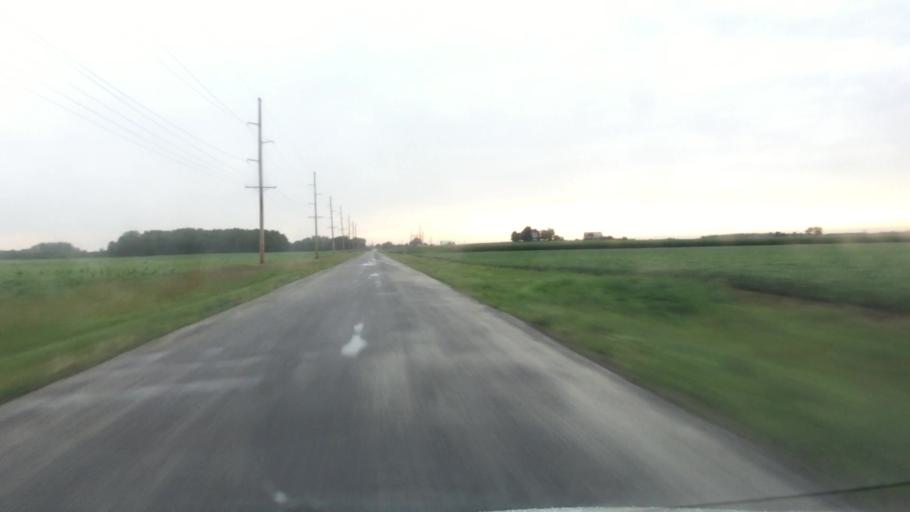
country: US
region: Iowa
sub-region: Lee County
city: Fort Madison
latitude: 40.5595
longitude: -91.2687
